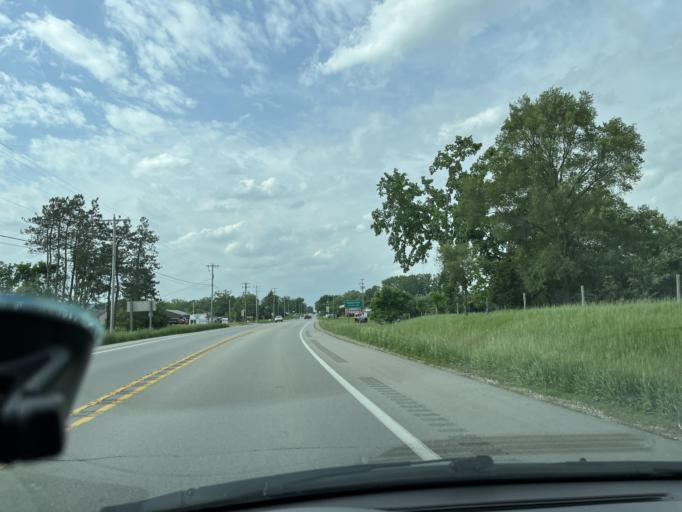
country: US
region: Michigan
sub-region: Barry County
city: Middleville
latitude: 42.7032
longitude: -85.4700
